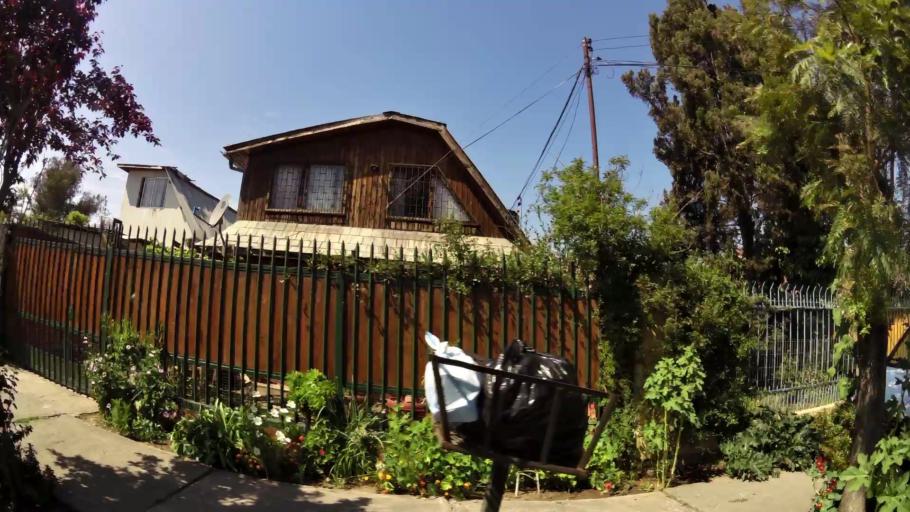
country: CL
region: Santiago Metropolitan
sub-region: Provincia de Santiago
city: La Pintana
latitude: -33.5320
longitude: -70.6555
